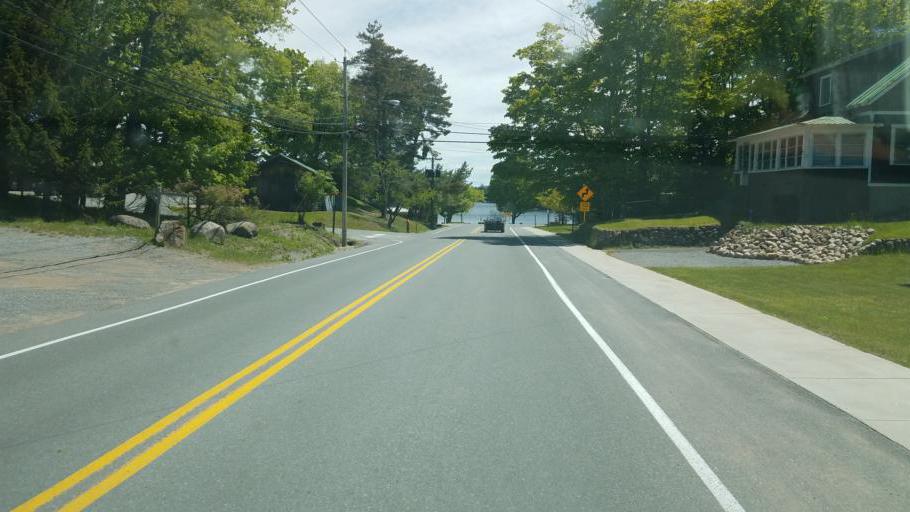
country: US
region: New York
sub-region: Oneida County
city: Boonville
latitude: 43.7091
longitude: -74.9725
